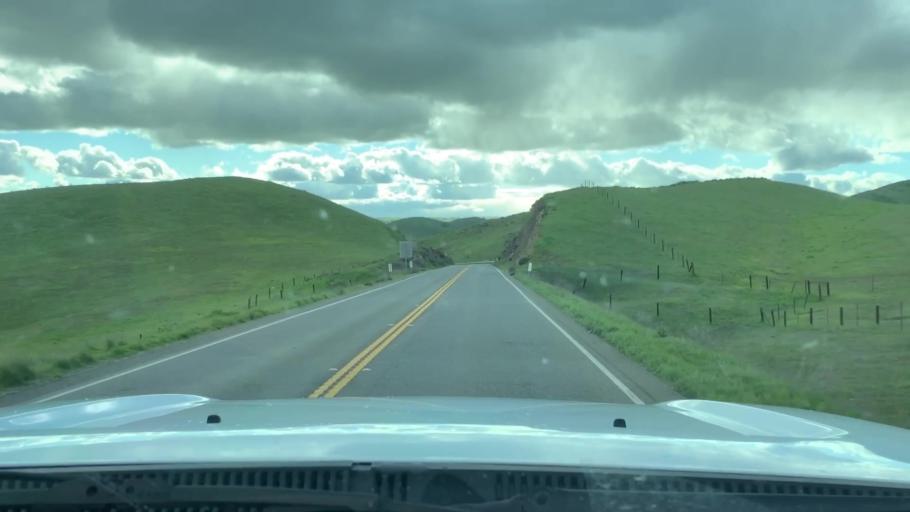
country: US
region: California
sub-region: San Luis Obispo County
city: Shandon
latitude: 35.7795
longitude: -120.2218
